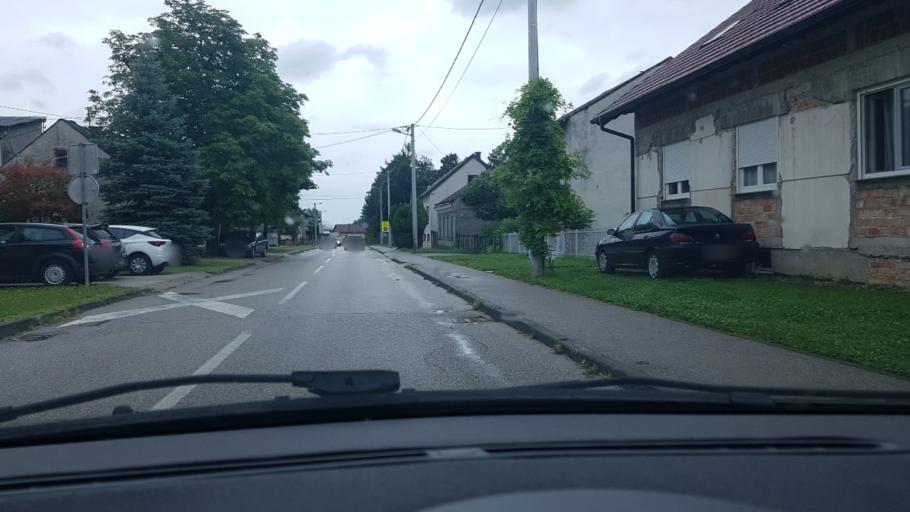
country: HR
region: Zagrebacka
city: Jastrebarsko
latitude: 45.6661
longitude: 15.6493
